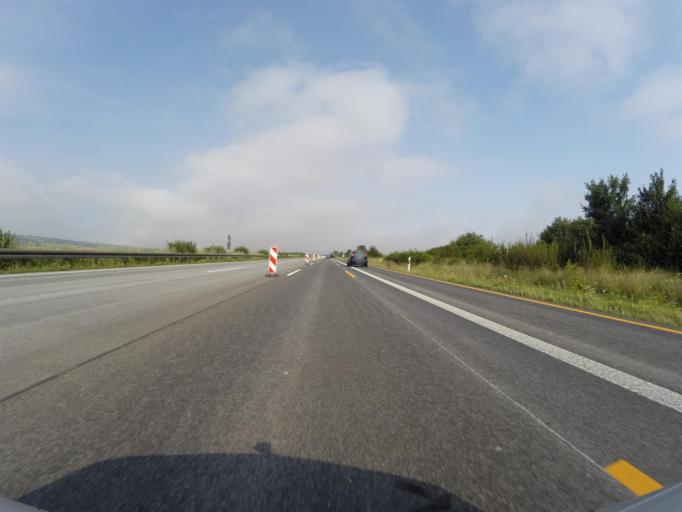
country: DE
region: Thuringia
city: Seebergen
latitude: 50.8808
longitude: 10.7902
